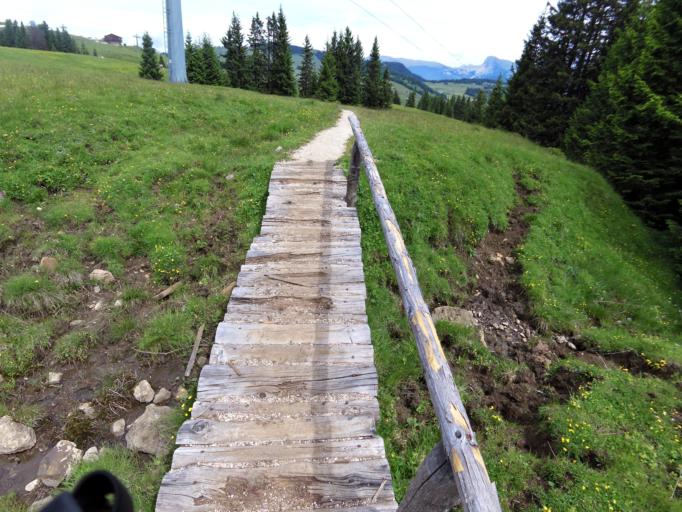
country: IT
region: Trentino-Alto Adige
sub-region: Bolzano
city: Ortisei
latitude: 46.5240
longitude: 11.6519
